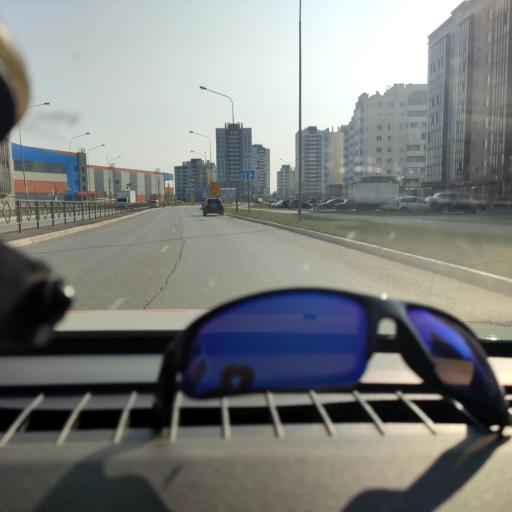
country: RU
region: Samara
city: Samara
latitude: 53.1102
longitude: 50.1409
